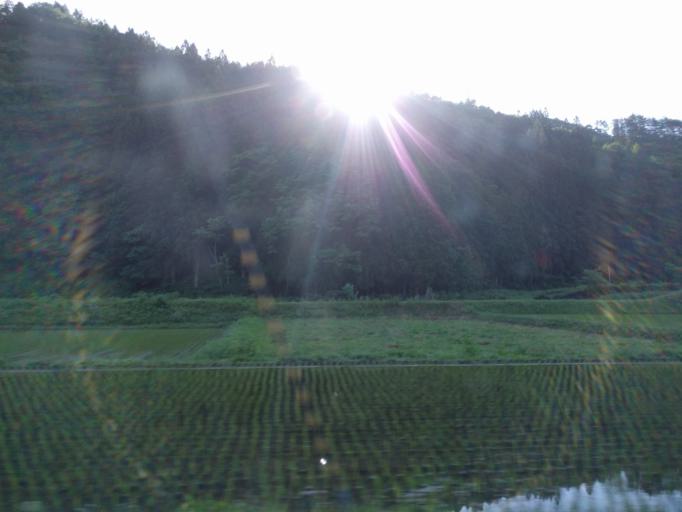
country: JP
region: Fukushima
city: Kitakata
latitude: 37.4115
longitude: 139.8096
